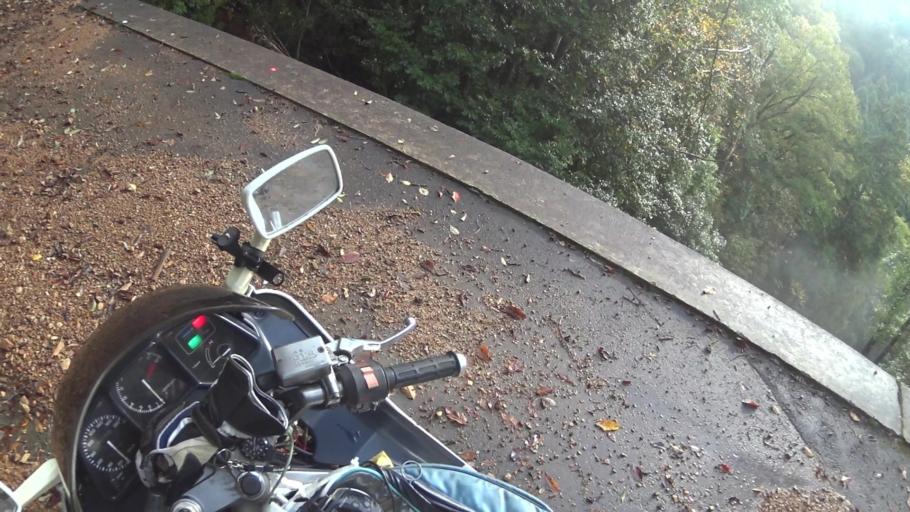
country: JP
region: Kyoto
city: Ayabe
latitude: 35.2696
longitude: 135.2266
